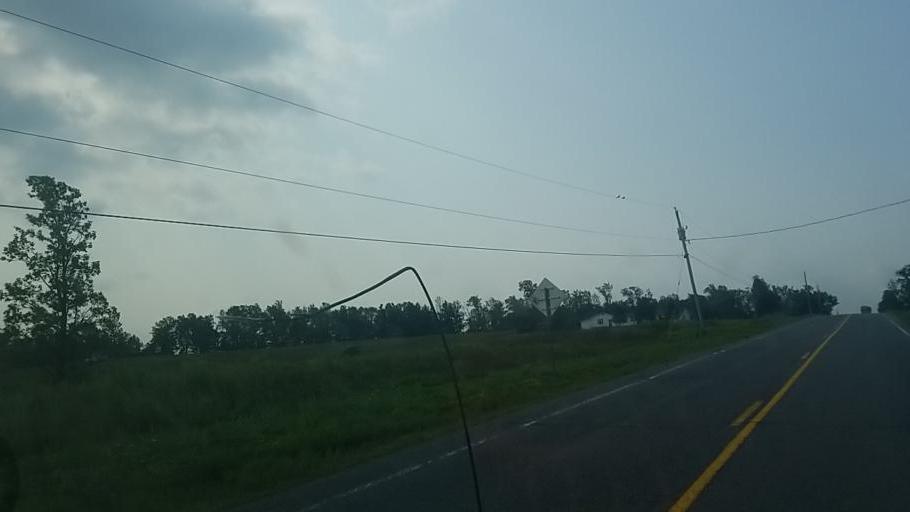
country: US
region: New York
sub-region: Fulton County
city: Johnstown
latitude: 43.0181
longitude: -74.4027
